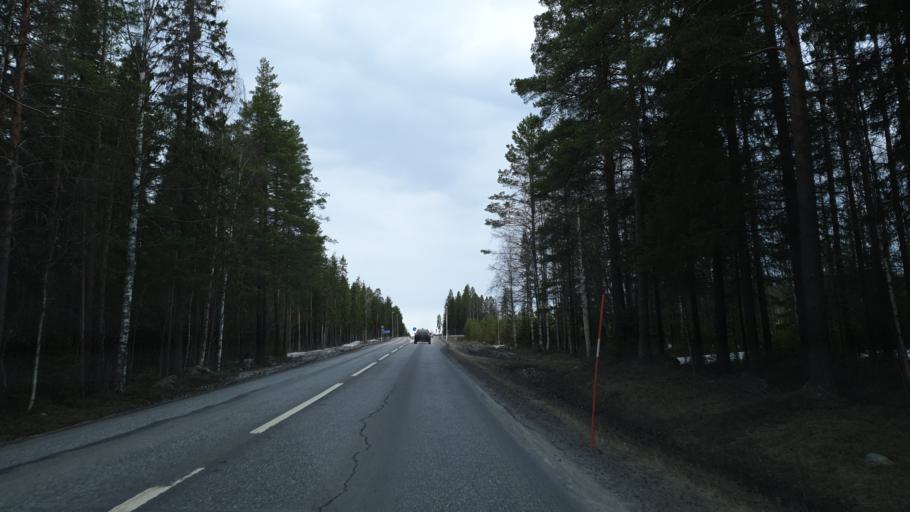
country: SE
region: Vaesterbotten
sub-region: Skelleftea Kommun
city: Viken
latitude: 64.6630
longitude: 20.9515
